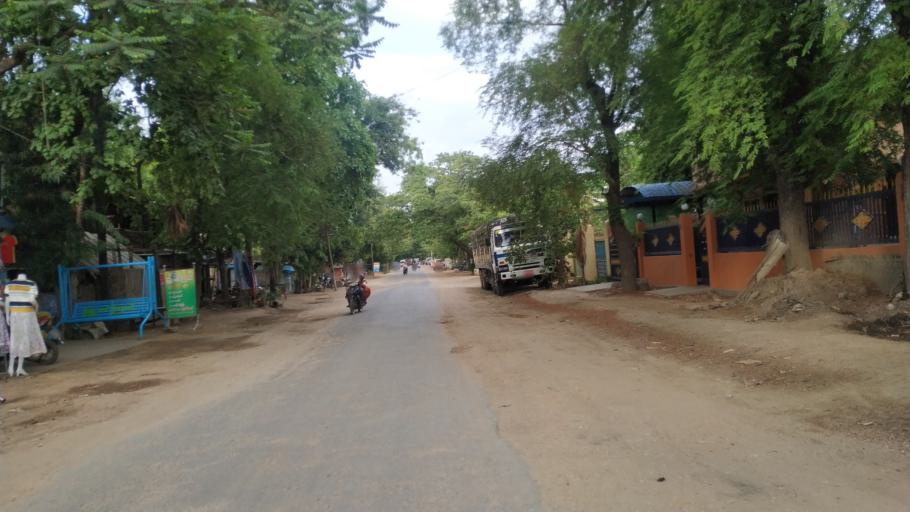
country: MM
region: Magway
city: Pakokku
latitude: 21.3356
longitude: 95.0733
